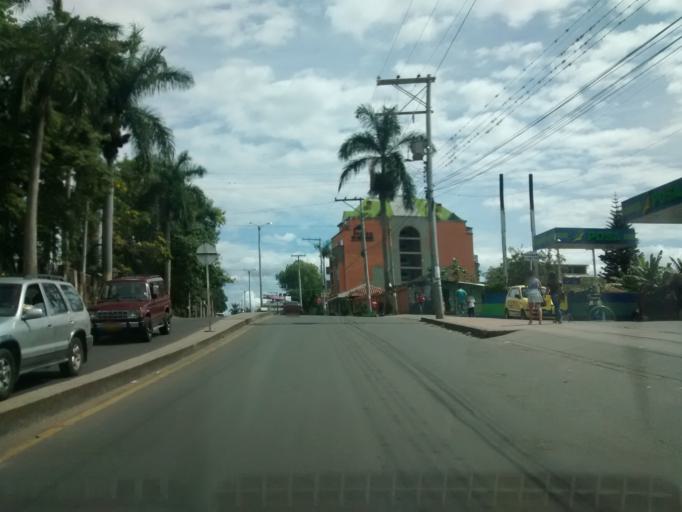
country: CO
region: Cundinamarca
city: Fusagasuga
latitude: 4.3389
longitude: -74.3640
